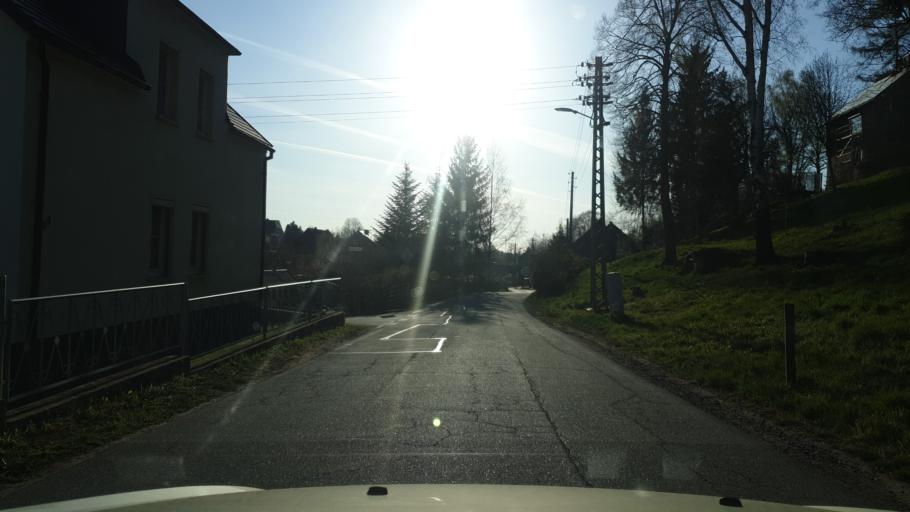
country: DE
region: Saxony
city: Kirchberg
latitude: 50.7610
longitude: 12.7568
